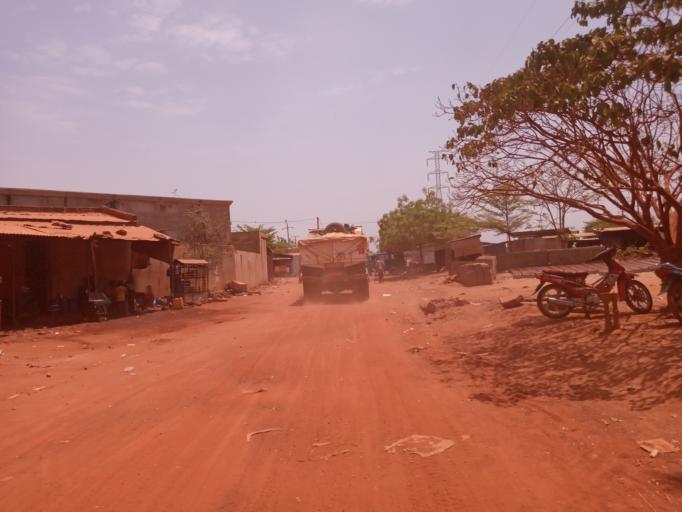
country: ML
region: Bamako
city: Bamako
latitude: 12.5579
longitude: -7.9802
